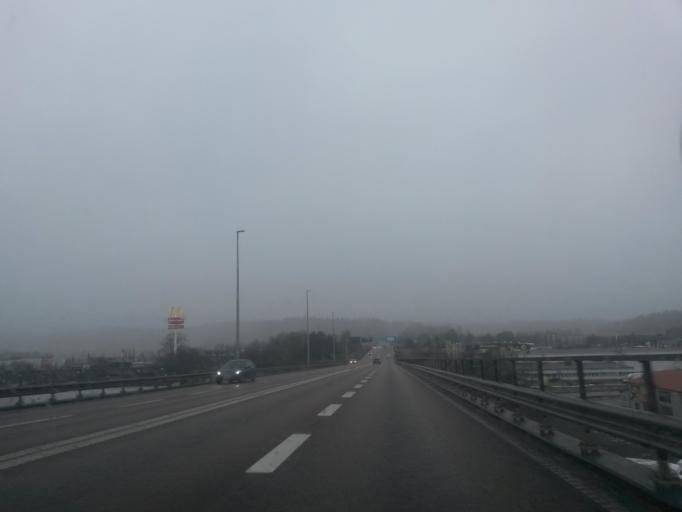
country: SE
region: Vaestra Goetaland
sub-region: Trollhattan
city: Trollhattan
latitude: 58.3134
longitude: 12.3118
